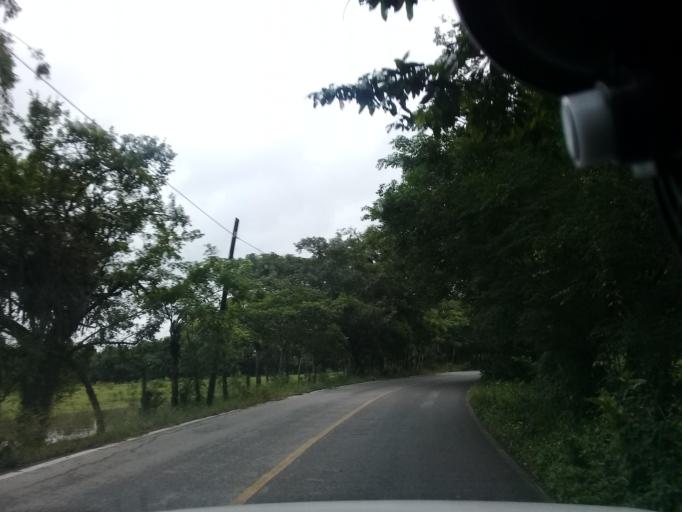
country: MX
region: Veracruz
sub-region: Chalma
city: San Pedro Coyutla
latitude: 21.2099
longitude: -98.4105
